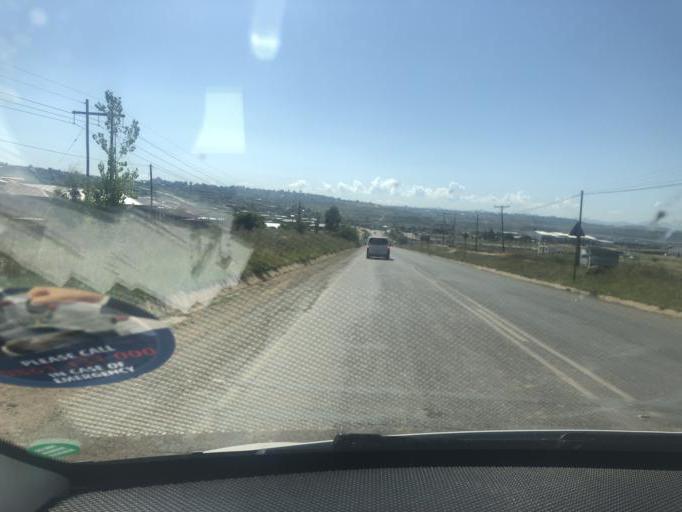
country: LS
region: Maseru
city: Maseru
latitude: -29.3760
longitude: 27.4803
